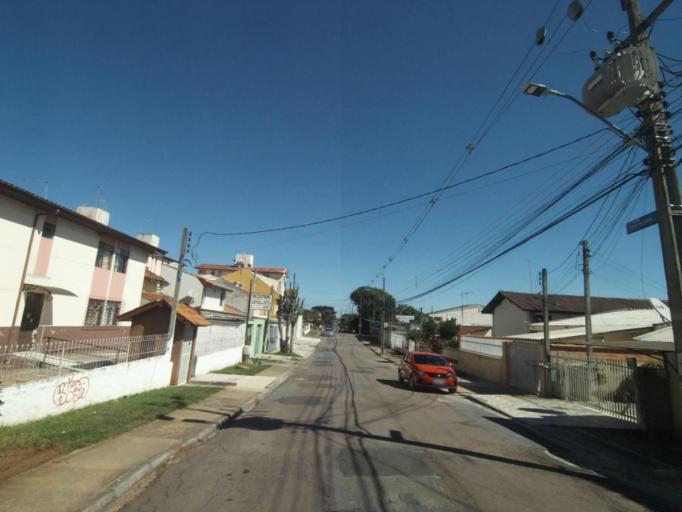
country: BR
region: Parana
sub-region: Curitiba
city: Curitiba
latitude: -25.4524
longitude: -49.3544
